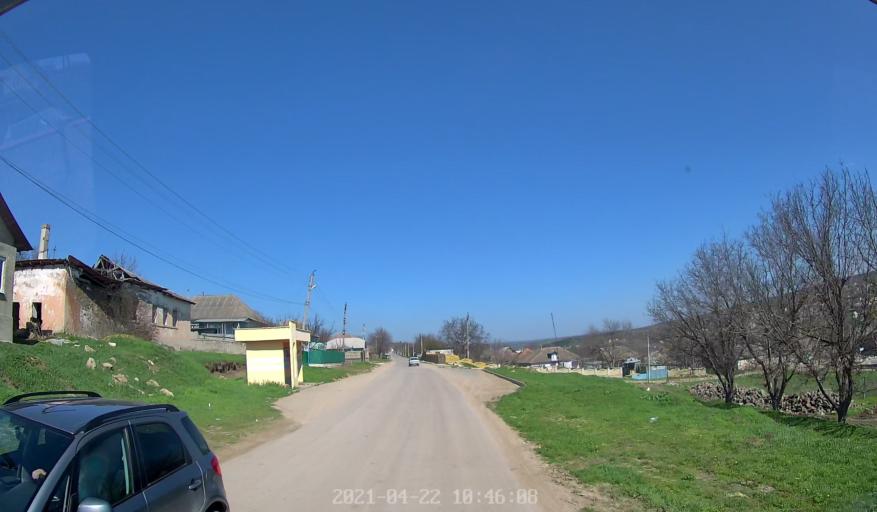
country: MD
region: Chisinau
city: Ciorescu
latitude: 47.1610
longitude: 28.9534
